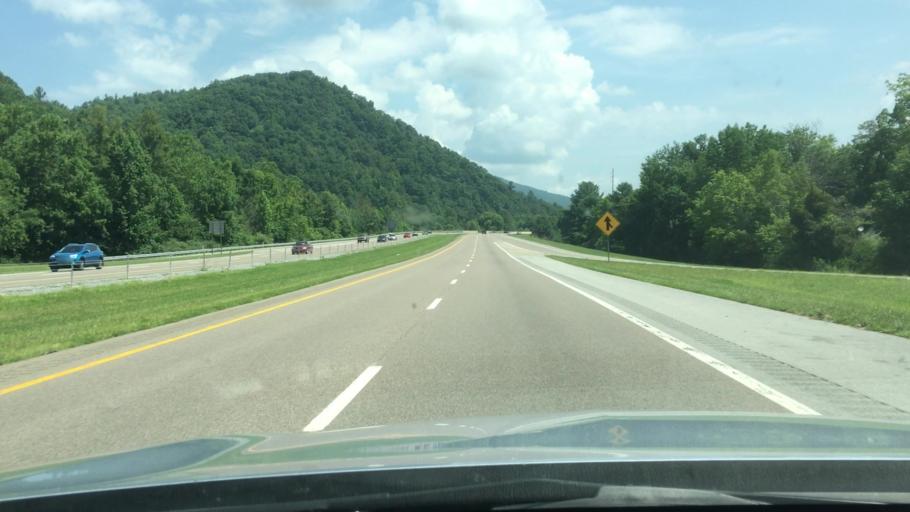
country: US
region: Tennessee
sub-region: Unicoi County
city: Erwin
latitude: 36.1660
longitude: -82.3964
